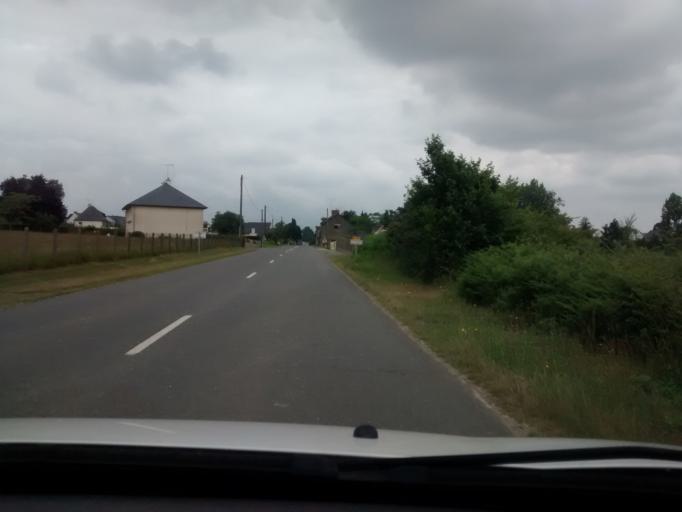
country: FR
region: Brittany
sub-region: Departement d'Ille-et-Vilaine
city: Liffre
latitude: 48.2016
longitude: -1.5103
